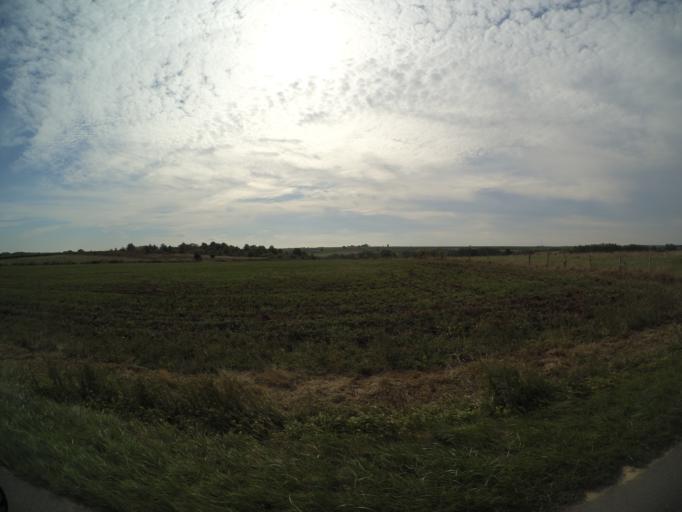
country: FR
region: Pays de la Loire
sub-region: Departement de Maine-et-Loire
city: Doue-la-Fontaine
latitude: 47.1926
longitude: -0.3277
